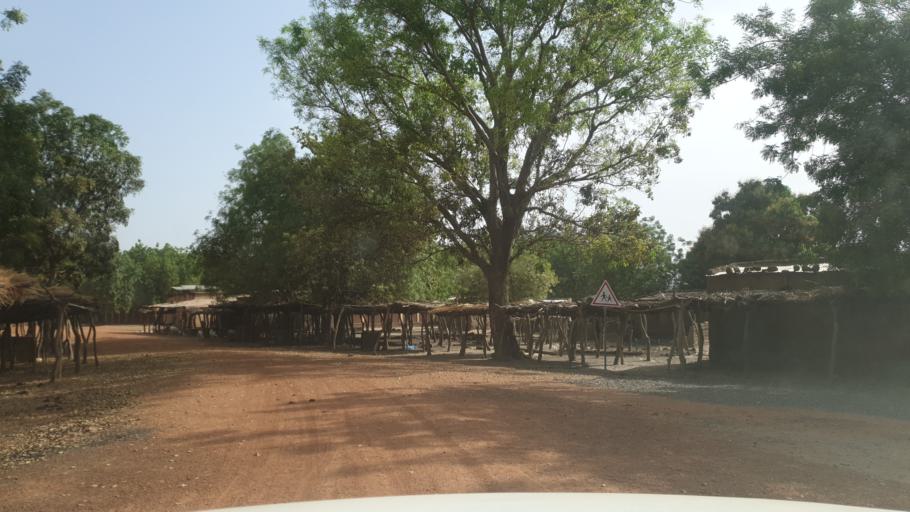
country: ML
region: Koulikoro
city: Kolokani
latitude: 13.3199
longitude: -8.2755
